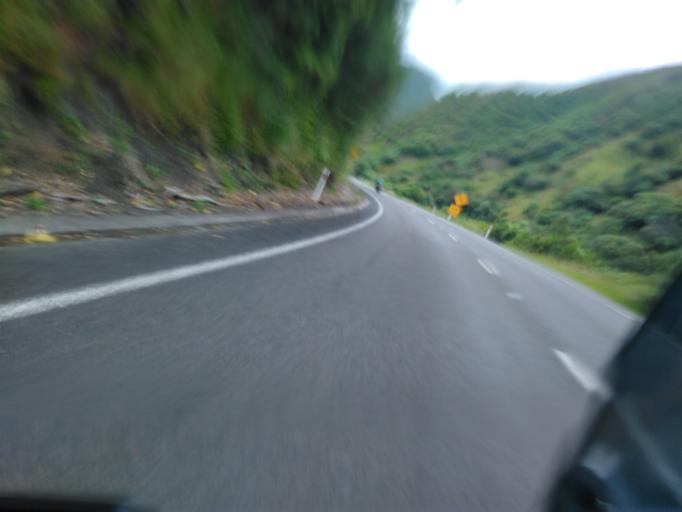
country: NZ
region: Bay of Plenty
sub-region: Opotiki District
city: Opotiki
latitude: -38.3371
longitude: 177.4212
